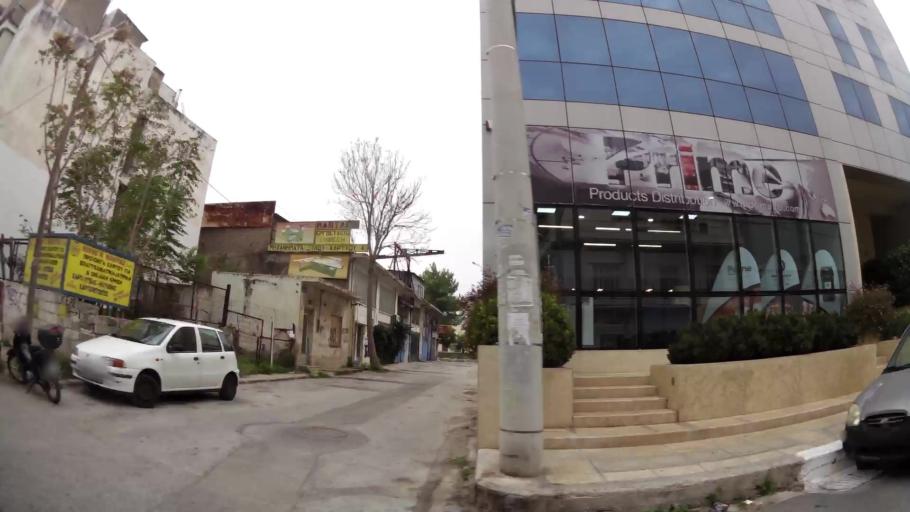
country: GR
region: Attica
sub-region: Nomos Piraios
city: Nikaia
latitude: 37.9561
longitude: 23.6556
